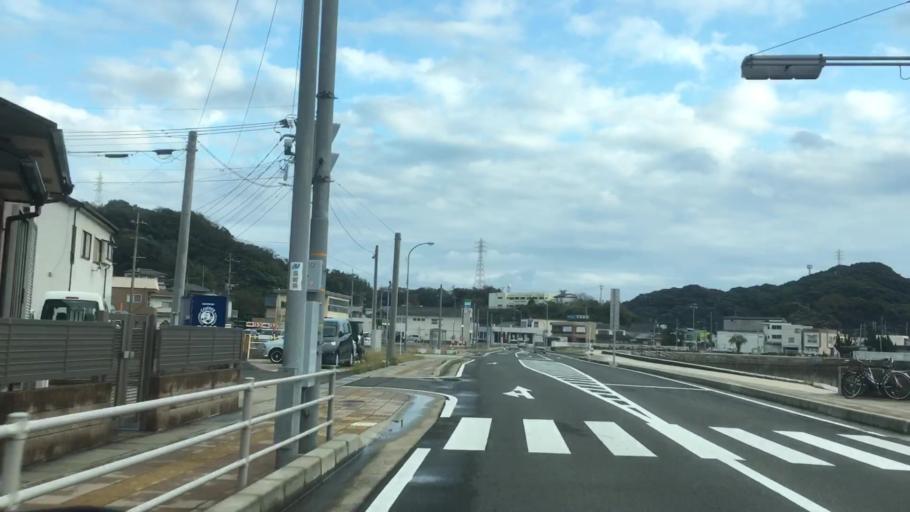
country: JP
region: Nagasaki
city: Togitsu
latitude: 32.9368
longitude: 129.6394
